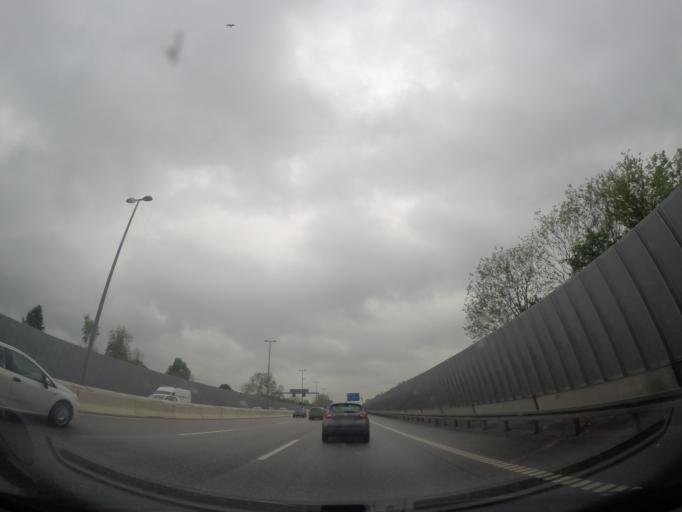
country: DK
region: Capital Region
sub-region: Herlev Kommune
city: Herlev
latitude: 55.7260
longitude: 12.4550
